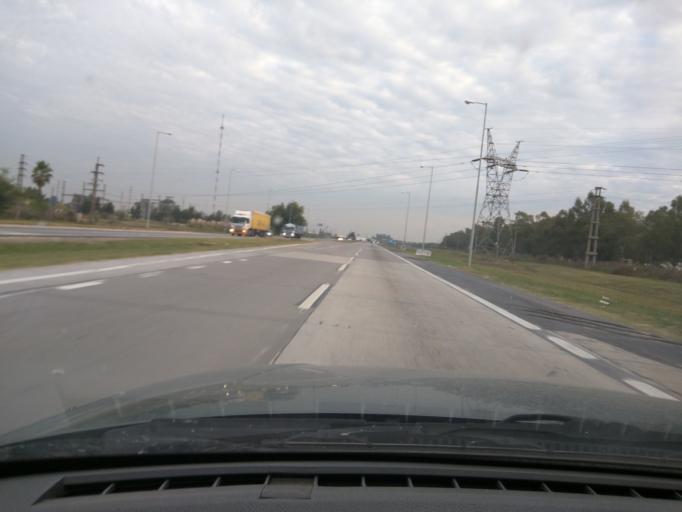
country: AR
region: Buenos Aires
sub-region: Partido de Campana
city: Campana
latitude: -34.2302
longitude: -58.9597
